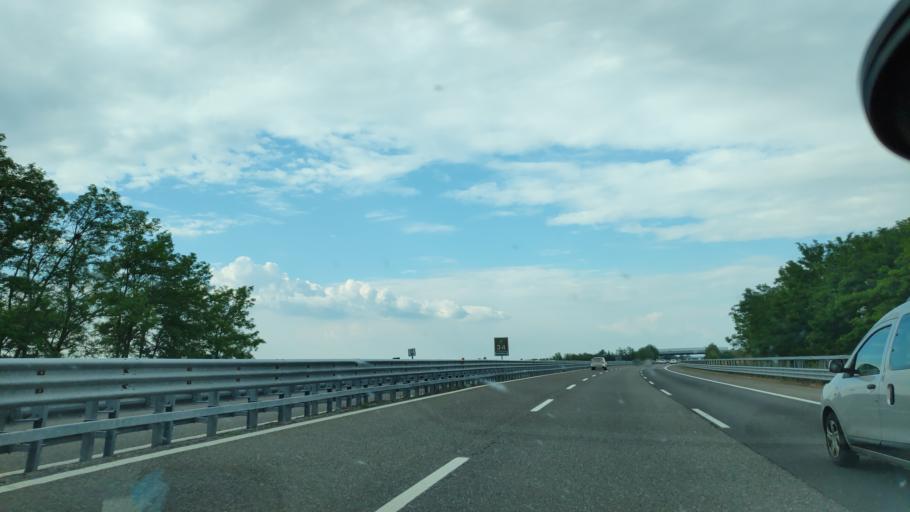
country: IT
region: Lombardy
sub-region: Provincia di Pavia
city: Pieve Albignola
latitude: 45.1263
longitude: 8.9783
